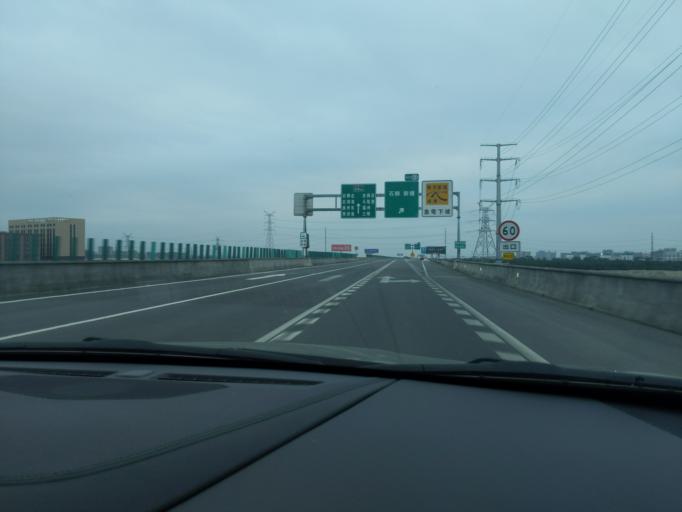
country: CN
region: Fujian
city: Xibin
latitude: 24.7703
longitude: 118.6209
